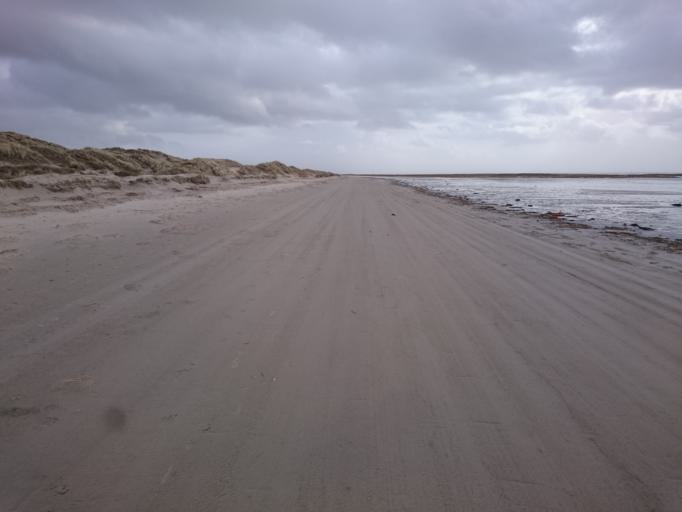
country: DK
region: South Denmark
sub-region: Fano Kommune
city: Nordby
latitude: 55.4305
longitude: 8.3654
